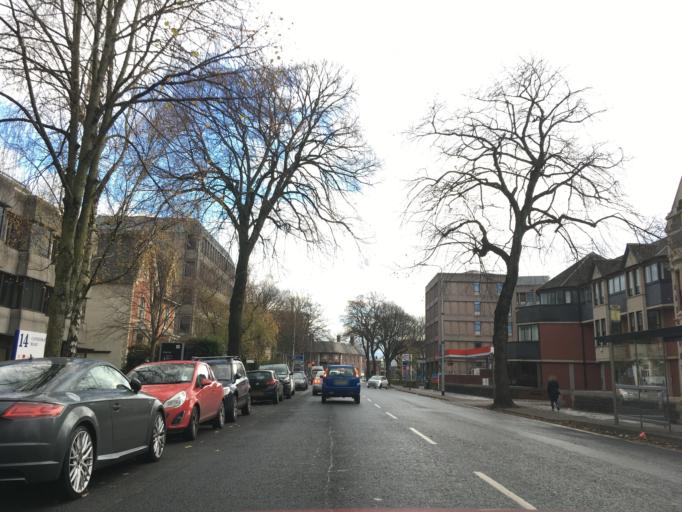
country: GB
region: Wales
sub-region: Cardiff
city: Cardiff
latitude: 51.4828
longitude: -3.1904
